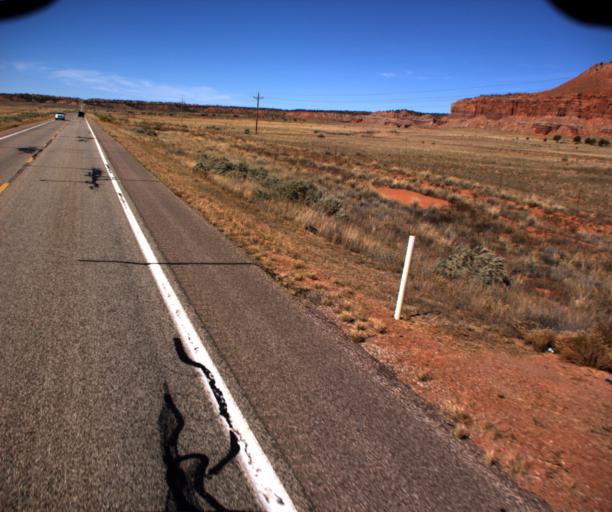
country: US
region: Arizona
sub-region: Mohave County
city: Colorado City
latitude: 36.8714
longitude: -112.8582
